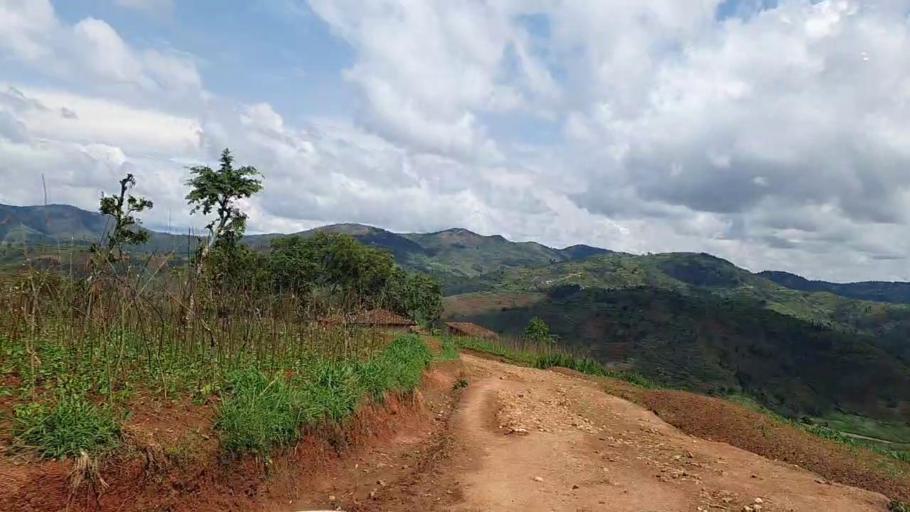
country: RW
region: Southern Province
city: Gikongoro
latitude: -2.3588
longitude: 29.5478
